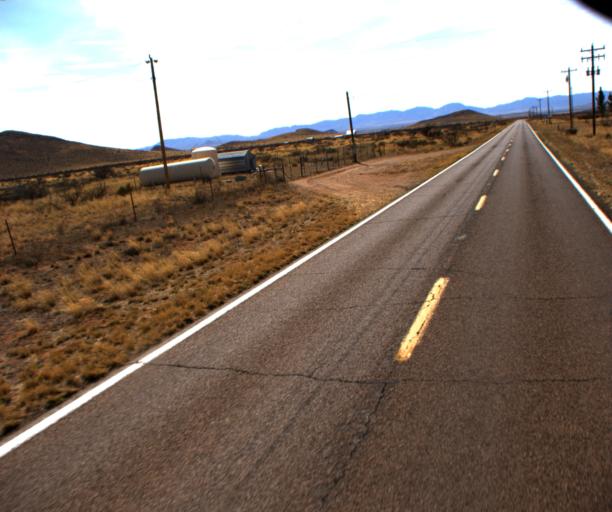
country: US
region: Arizona
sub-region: Cochise County
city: Willcox
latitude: 31.8765
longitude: -109.6522
